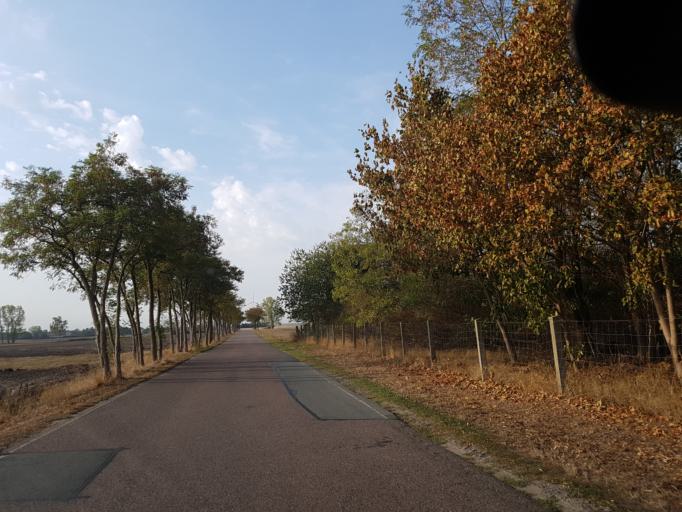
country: DE
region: Saxony
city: Wulknitz
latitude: 51.3795
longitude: 13.3871
